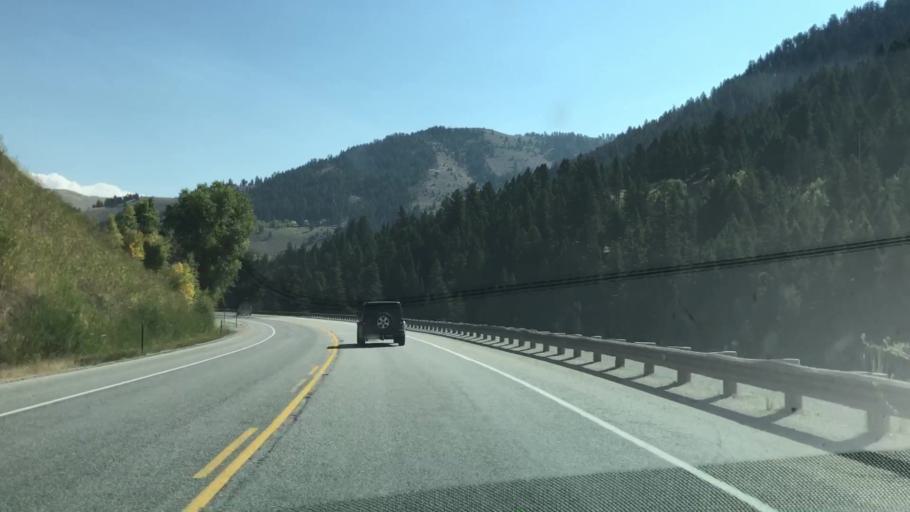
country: US
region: Wyoming
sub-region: Teton County
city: Hoback
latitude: 43.3008
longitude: -110.7579
